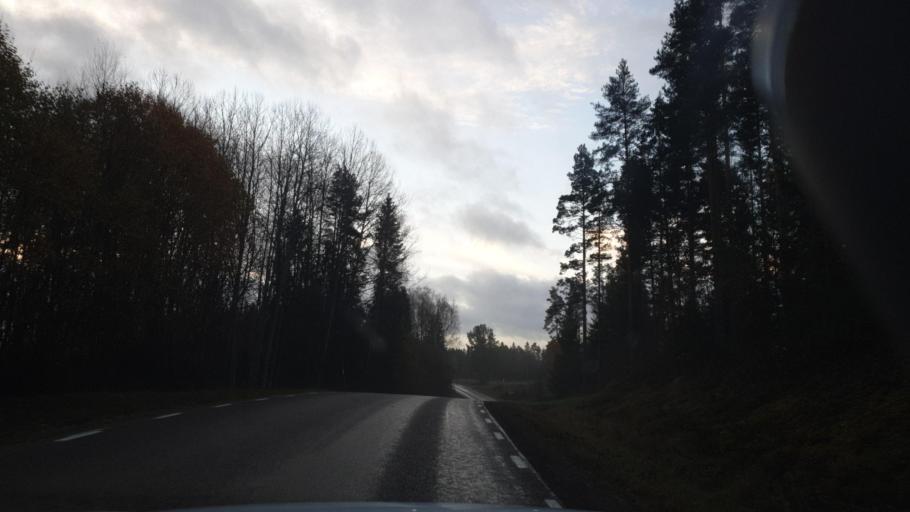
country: SE
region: Vaermland
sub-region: Arvika Kommun
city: Arvika
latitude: 59.6315
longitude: 12.7979
